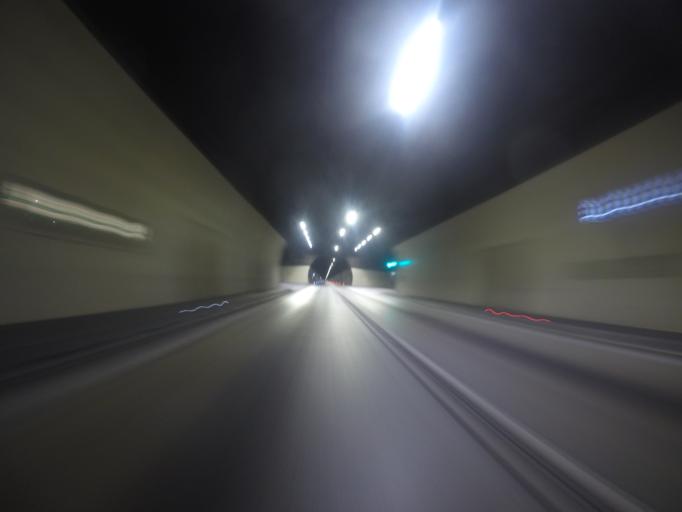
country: ME
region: Bar
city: Sutomore
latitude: 42.1547
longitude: 19.0047
